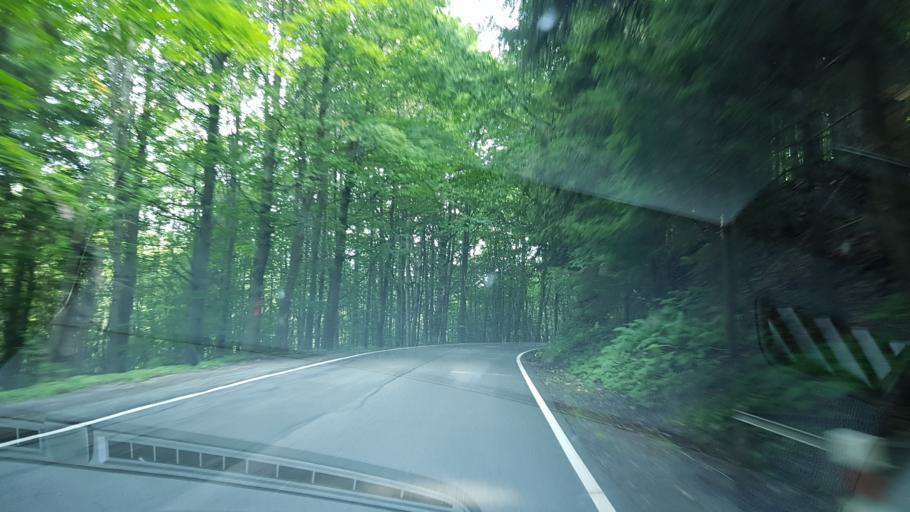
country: CZ
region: Olomoucky
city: Ceska Ves
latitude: 50.2167
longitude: 17.2499
